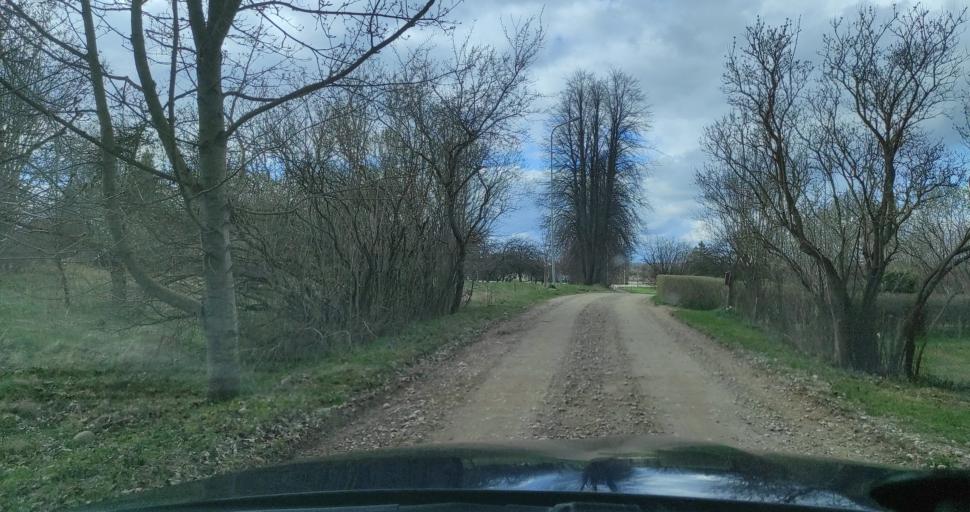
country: LV
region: Aizpute
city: Aizpute
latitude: 56.7166
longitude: 21.5866
